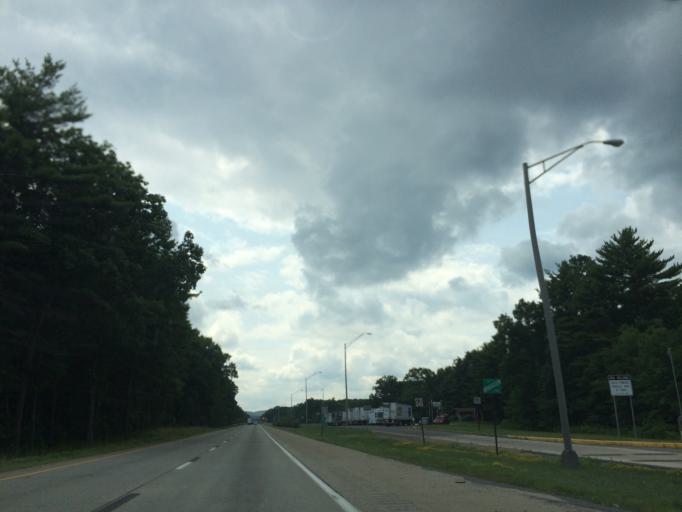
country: US
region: Pennsylvania
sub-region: Luzerne County
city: Nanticoke
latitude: 41.1323
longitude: -75.9631
